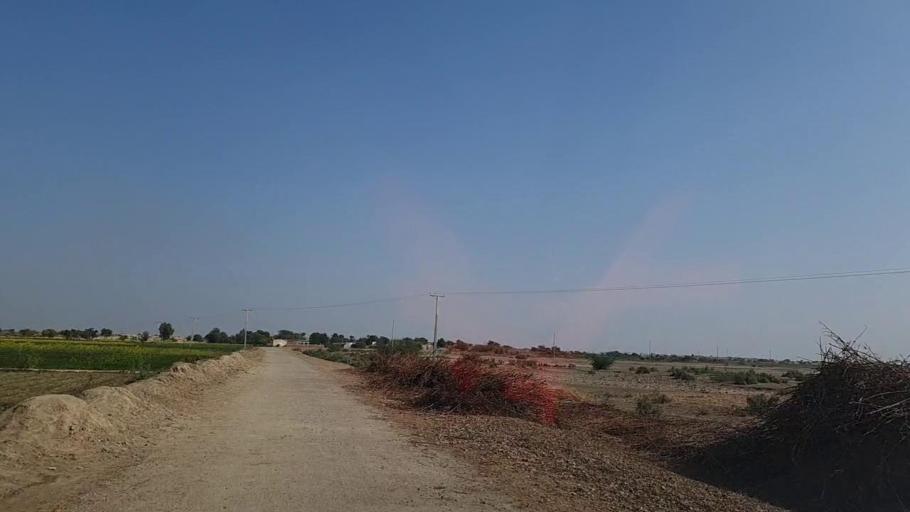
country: PK
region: Sindh
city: Tando Mittha Khan
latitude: 26.0282
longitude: 69.1159
